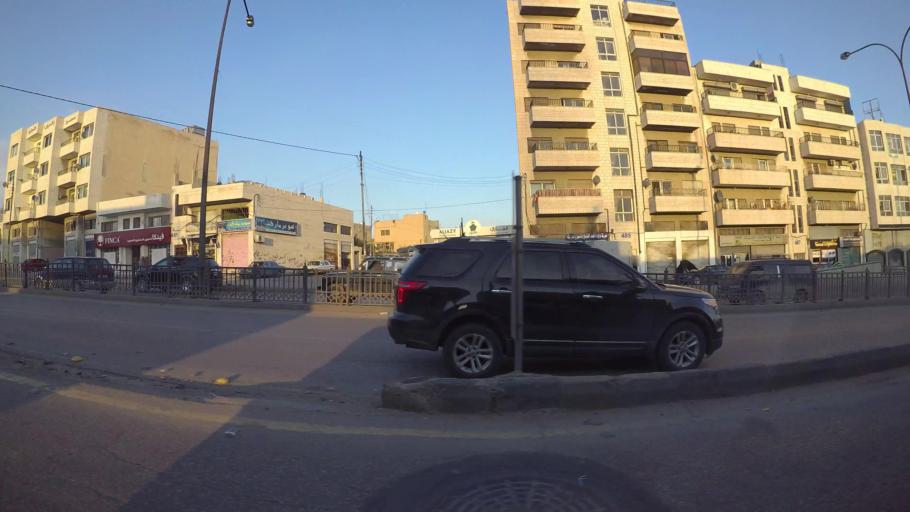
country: JO
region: Amman
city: Al Quwaysimah
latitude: 31.9032
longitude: 35.9372
